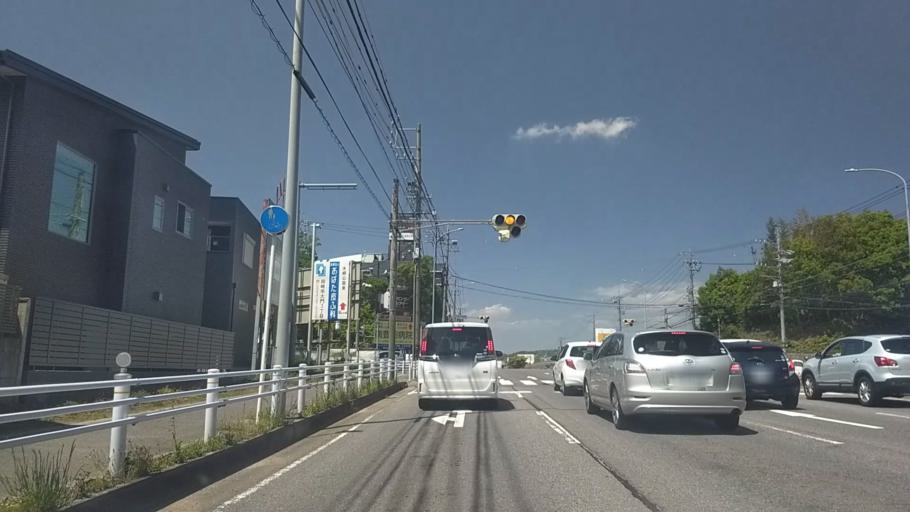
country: JP
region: Aichi
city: Okazaki
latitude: 34.9540
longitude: 137.1898
